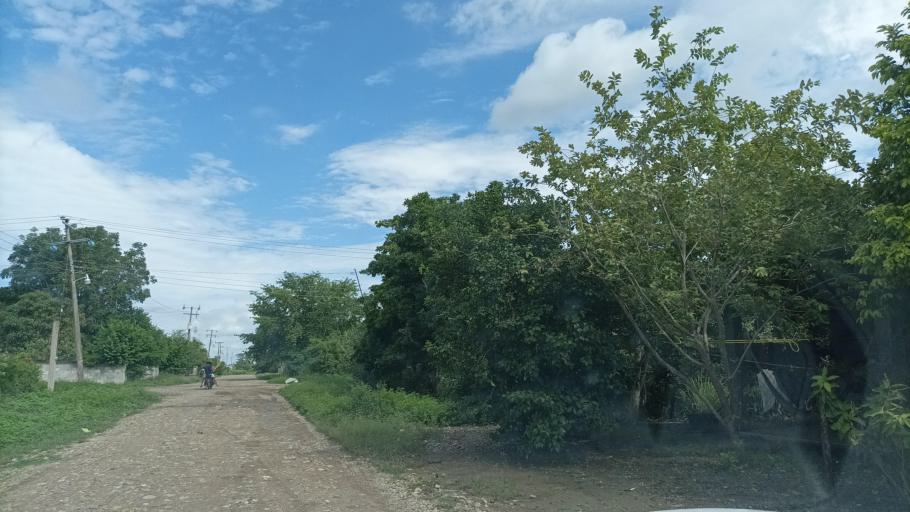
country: MX
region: Veracruz
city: Panuco
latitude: 21.9443
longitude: -98.1374
